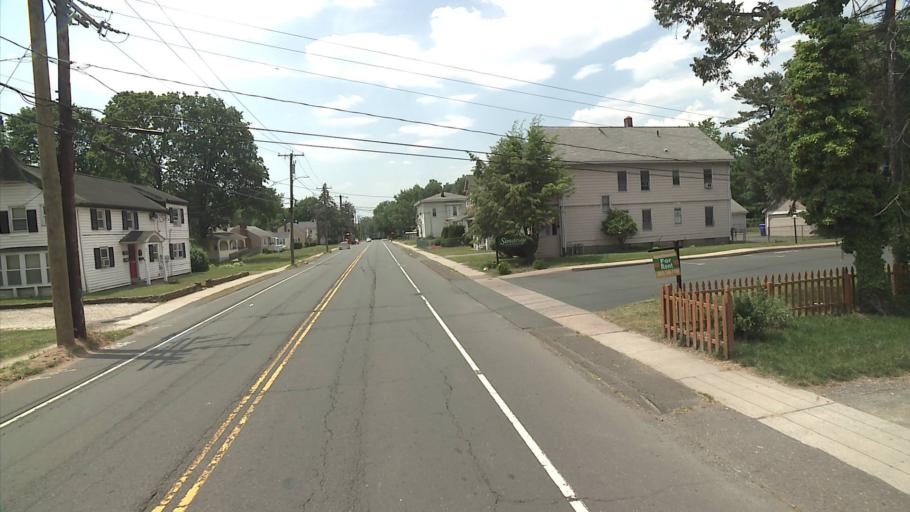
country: US
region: Connecticut
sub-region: Hartford County
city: East Hartford
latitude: 41.7610
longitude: -72.6401
